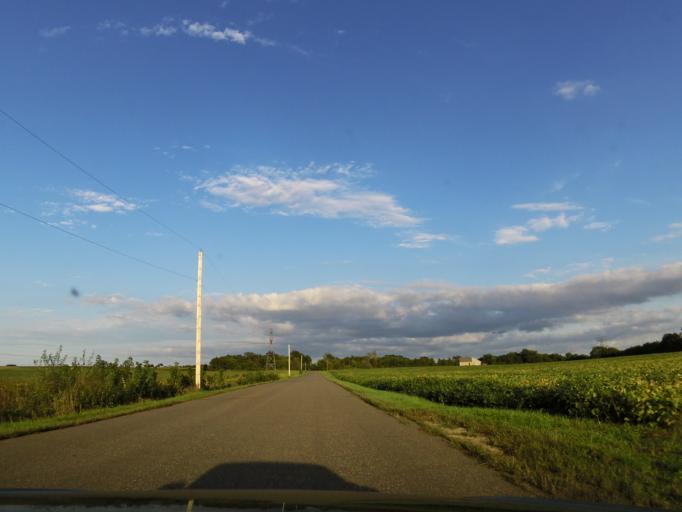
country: US
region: Minnesota
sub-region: Washington County
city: Afton
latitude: 44.8765
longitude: -92.8589
